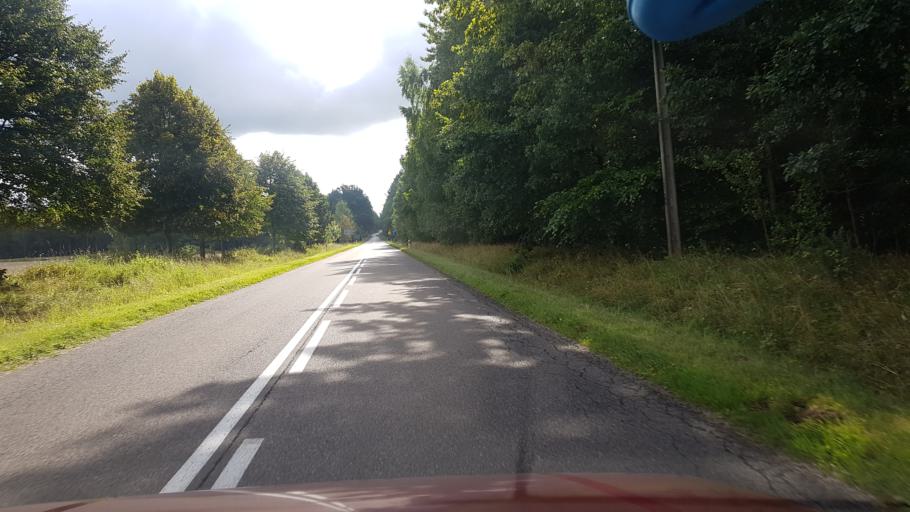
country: PL
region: West Pomeranian Voivodeship
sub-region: Powiat koszalinski
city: Polanow
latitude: 54.1062
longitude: 16.7955
